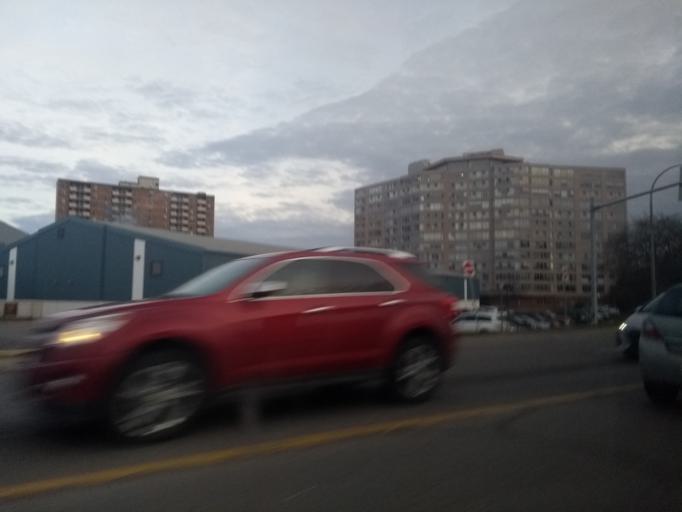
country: CA
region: Ontario
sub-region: Regional Municipality of Niagara
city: St. Catharines
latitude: 43.1608
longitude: -79.2402
